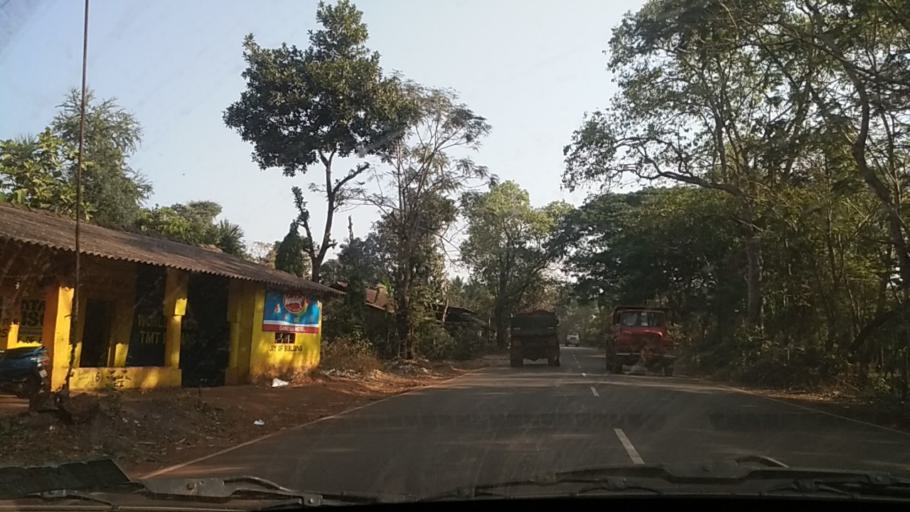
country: IN
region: Goa
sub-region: South Goa
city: Sanvordem
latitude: 15.2855
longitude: 74.1291
